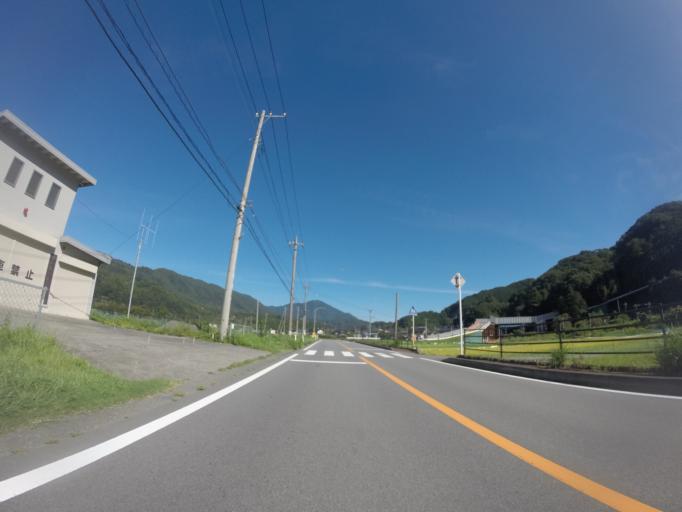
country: JP
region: Shizuoka
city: Fujinomiya
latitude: 35.3299
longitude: 138.4515
